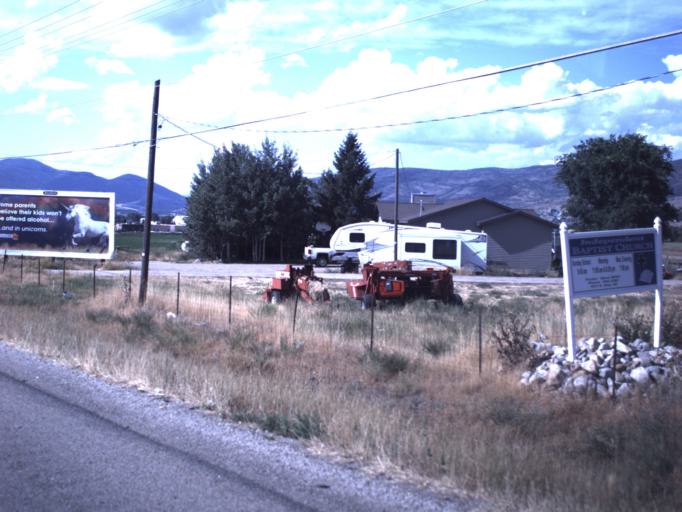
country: US
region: Utah
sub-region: Wasatch County
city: Heber
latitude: 40.4850
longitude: -111.4052
